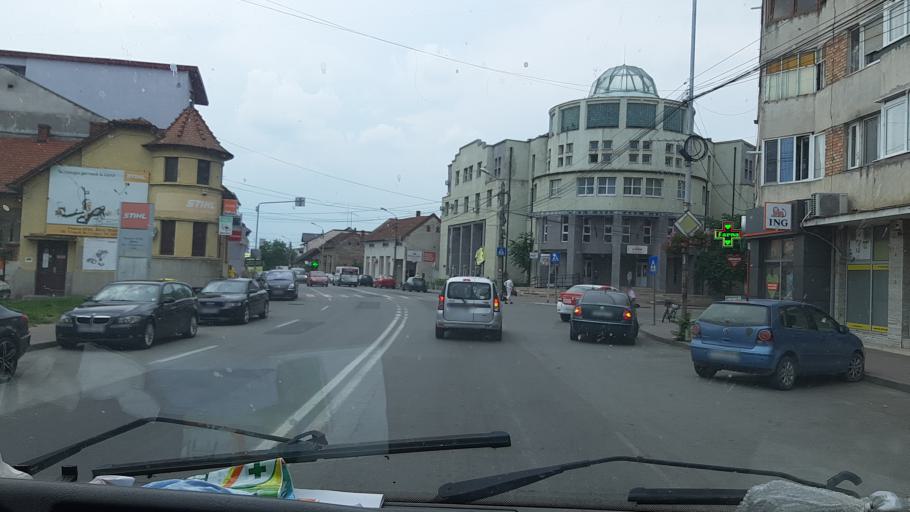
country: RO
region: Timis
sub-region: Municipiul Lugoj
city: Lugoj
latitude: 45.6907
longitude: 21.9030
